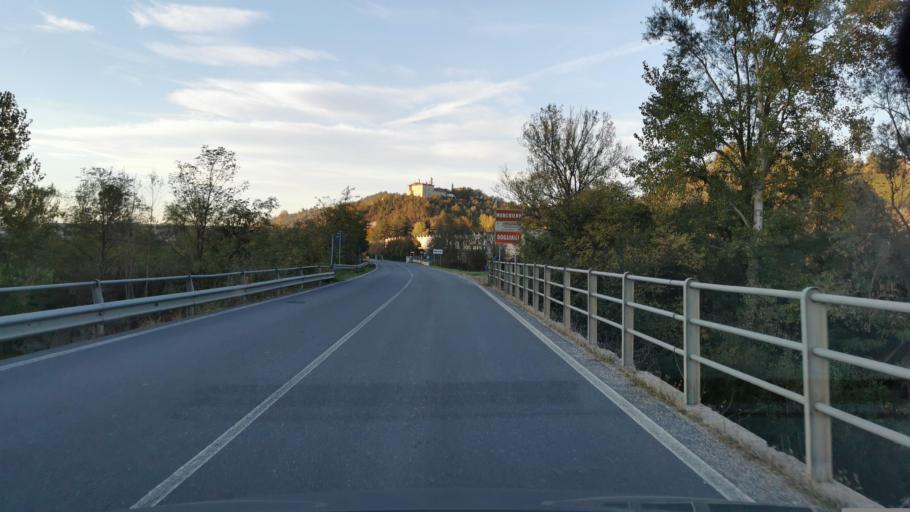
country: IT
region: Piedmont
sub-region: Provincia di Cuneo
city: Monchiero Borgonuovo
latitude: 44.5605
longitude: 7.9229
